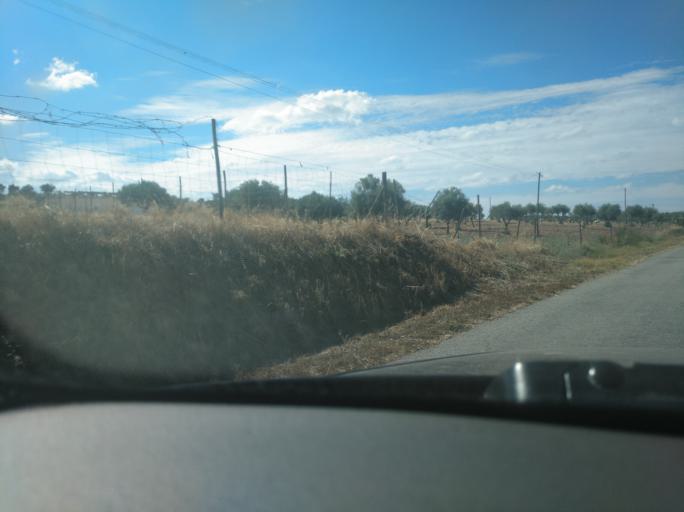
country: ES
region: Extremadura
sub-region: Provincia de Badajoz
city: La Codosera
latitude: 39.1505
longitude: -7.1591
